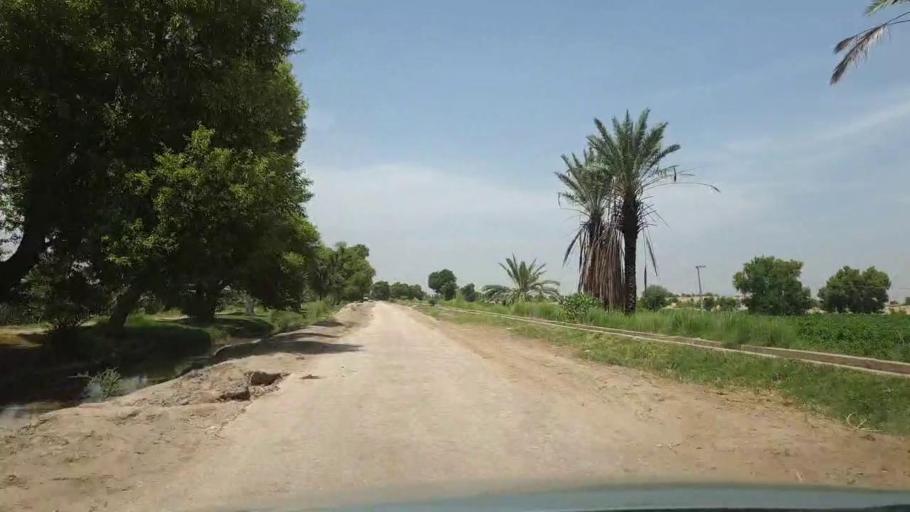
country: PK
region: Sindh
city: Kot Diji
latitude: 27.1348
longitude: 69.0209
